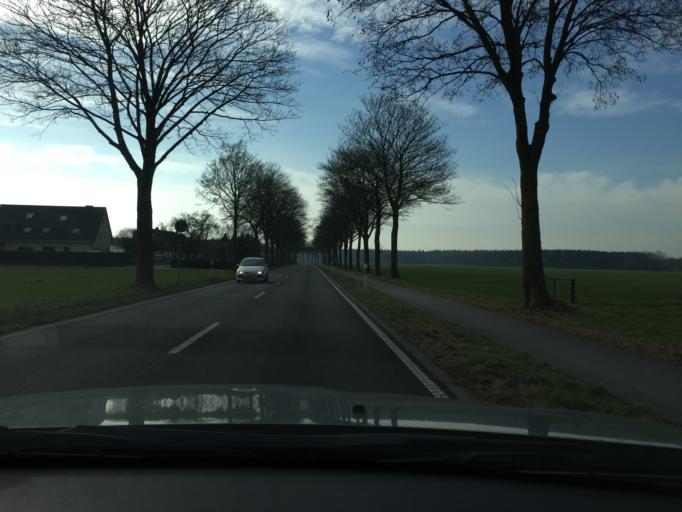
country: DE
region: North Rhine-Westphalia
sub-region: Regierungsbezirk Dusseldorf
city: Kleve
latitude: 51.7529
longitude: 6.1275
